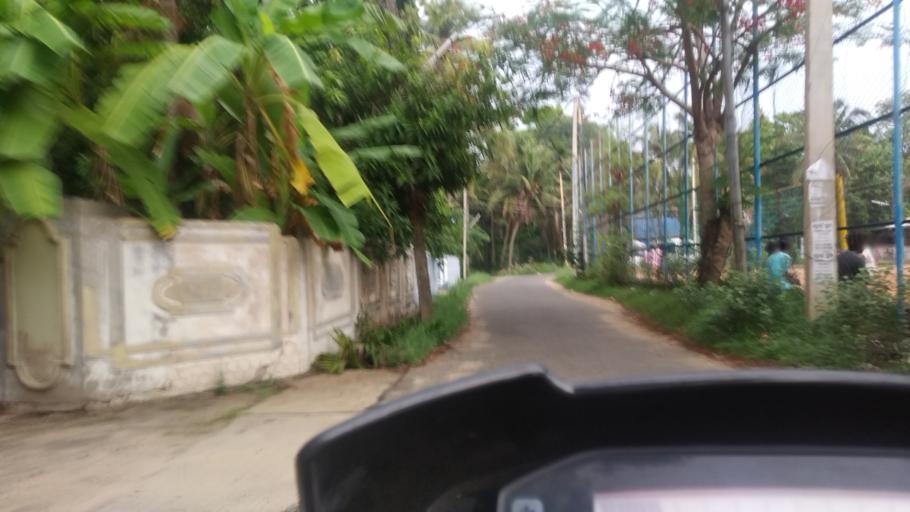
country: IN
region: Kerala
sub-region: Ernakulam
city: Elur
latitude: 10.0634
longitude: 76.2143
